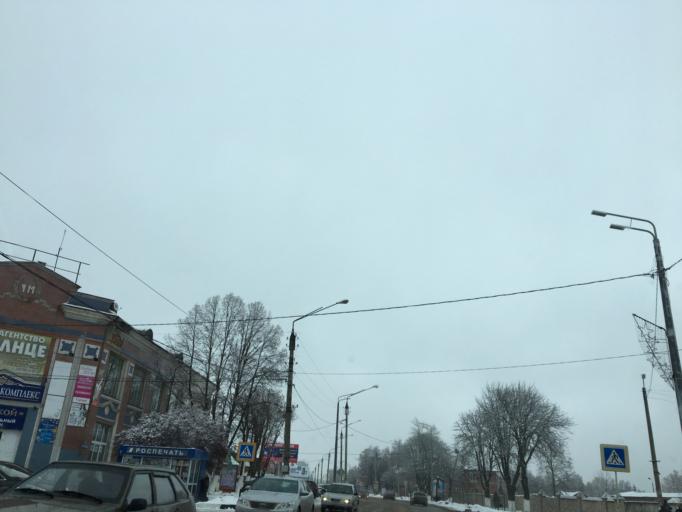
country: RU
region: Tula
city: Donskoy
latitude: 53.9671
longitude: 38.3156
